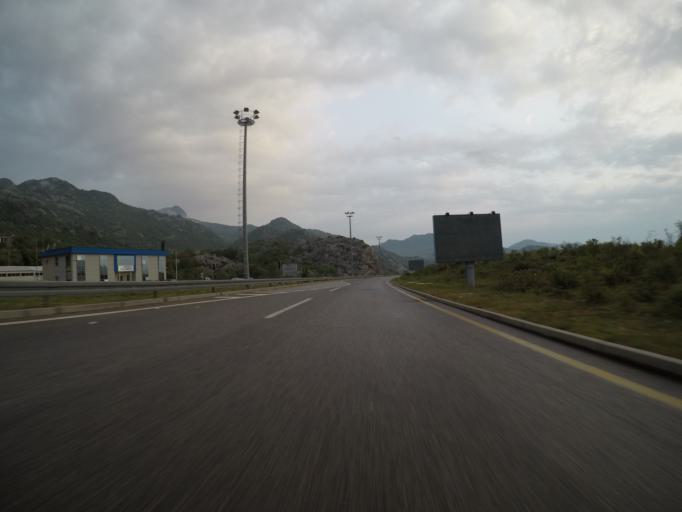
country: ME
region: Bar
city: Sutomore
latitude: 42.2025
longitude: 19.0509
